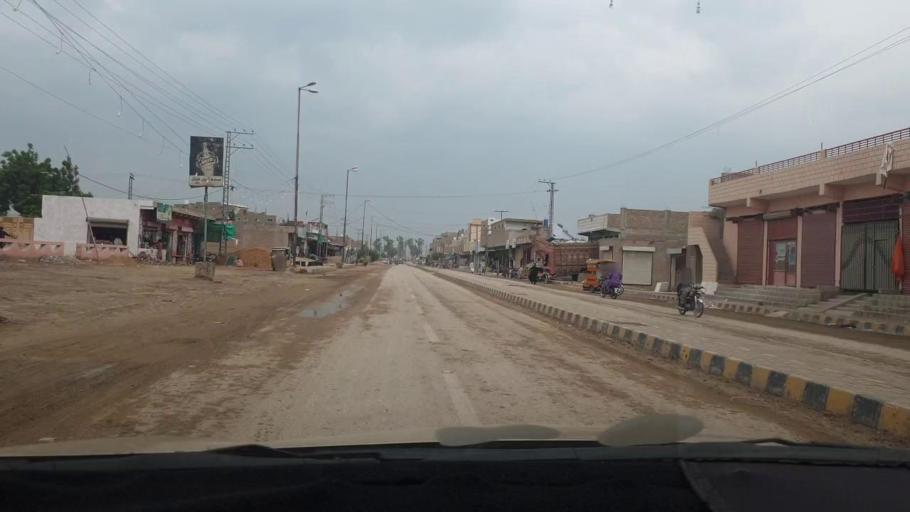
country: PK
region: Sindh
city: Larkana
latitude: 27.5749
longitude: 68.2283
